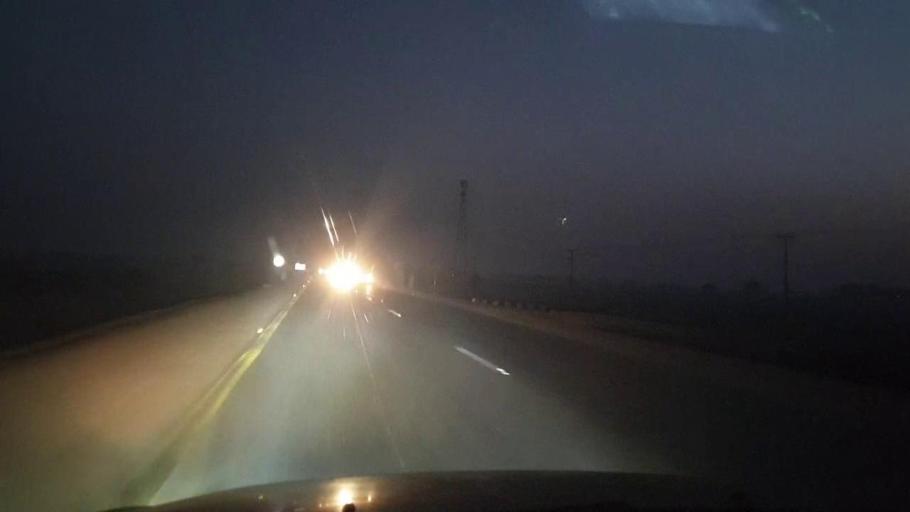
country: PK
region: Sindh
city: Chambar
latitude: 25.3341
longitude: 68.7969
